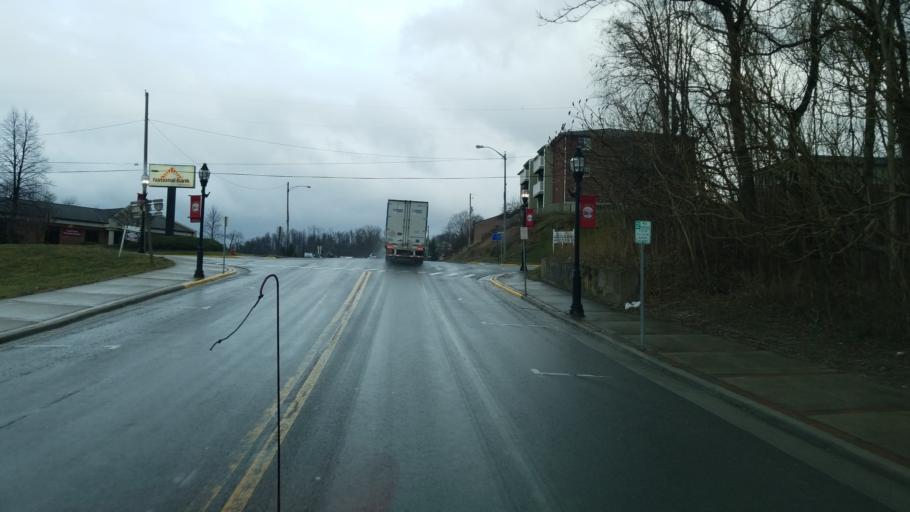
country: US
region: Virginia
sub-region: Giles County
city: Pearisburg
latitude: 37.3257
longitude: -80.7347
